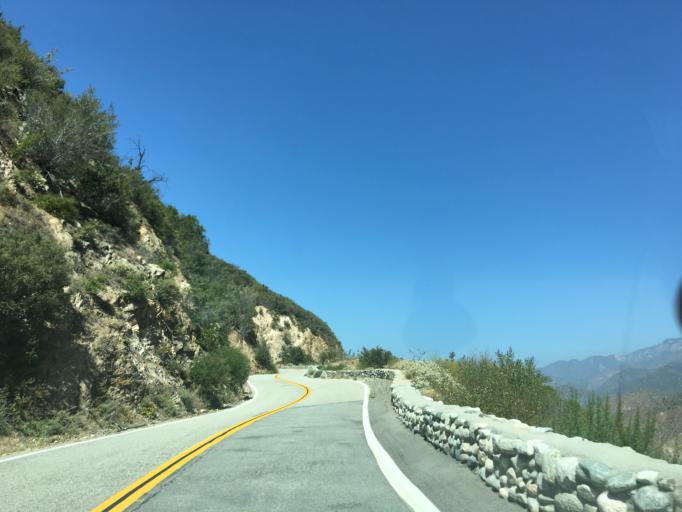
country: US
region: California
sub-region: Los Angeles County
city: Glendora
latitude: 34.2282
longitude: -117.7837
